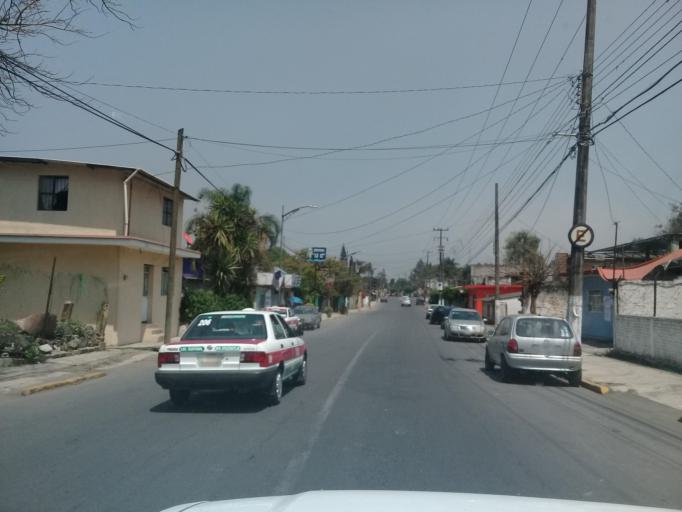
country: MX
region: Veracruz
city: Ixtac Zoquitlan
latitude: 18.8680
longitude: -97.0606
